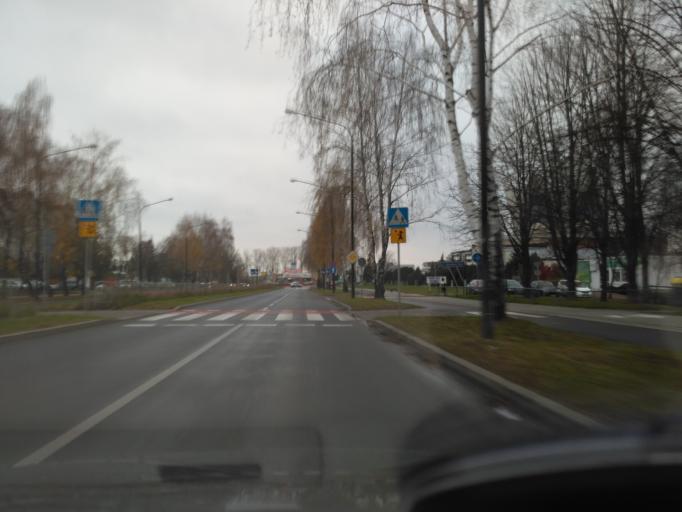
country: PL
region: Lublin Voivodeship
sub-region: Powiat lubelski
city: Lublin
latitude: 51.2671
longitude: 22.5457
